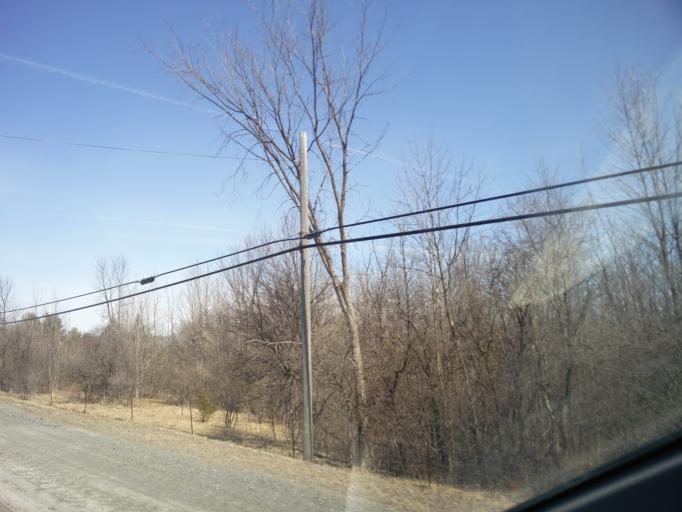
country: CA
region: Ontario
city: Ottawa
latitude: 45.1970
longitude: -75.6435
